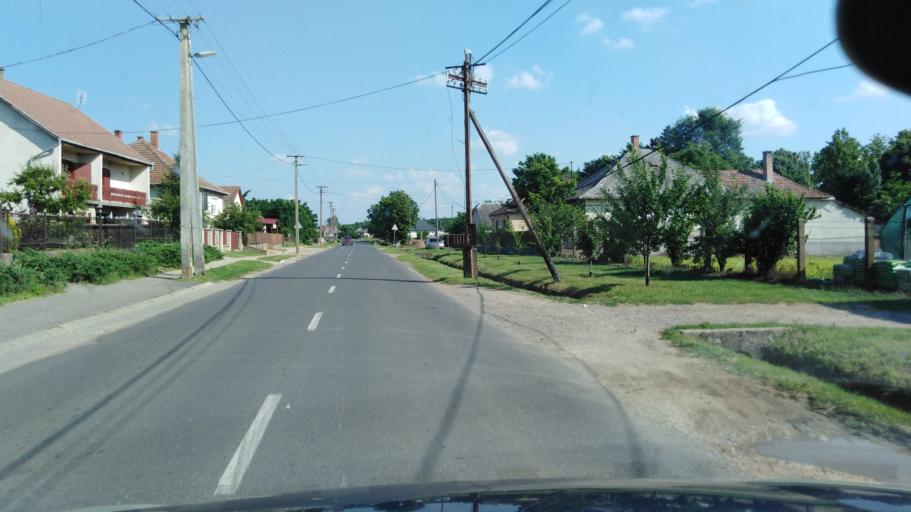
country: HU
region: Szabolcs-Szatmar-Bereg
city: Nyirvasvari
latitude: 47.8181
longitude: 22.1911
